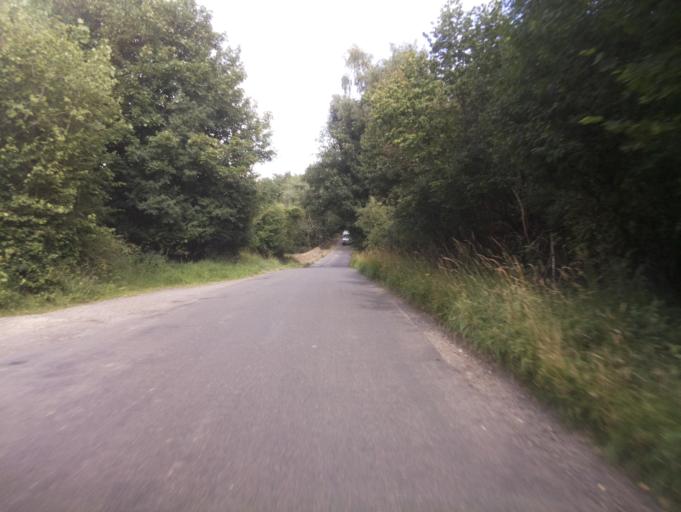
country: GB
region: England
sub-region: Gloucestershire
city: Coates
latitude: 51.7395
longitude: -2.0407
